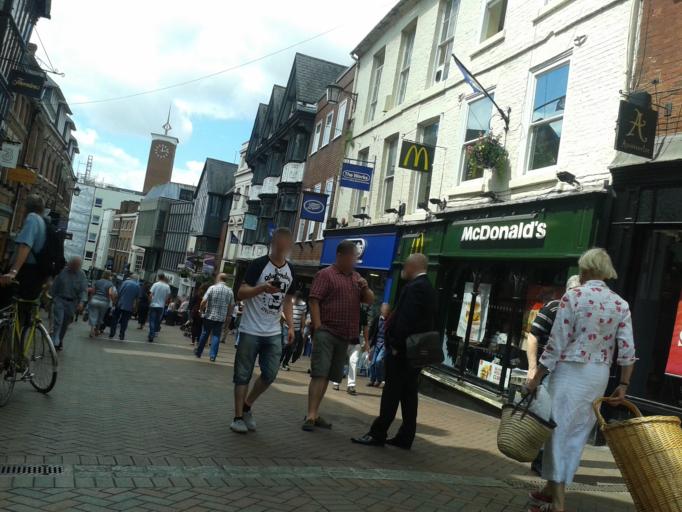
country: GB
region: England
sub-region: Shropshire
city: Shrewsbury
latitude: 52.7084
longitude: -2.7533
